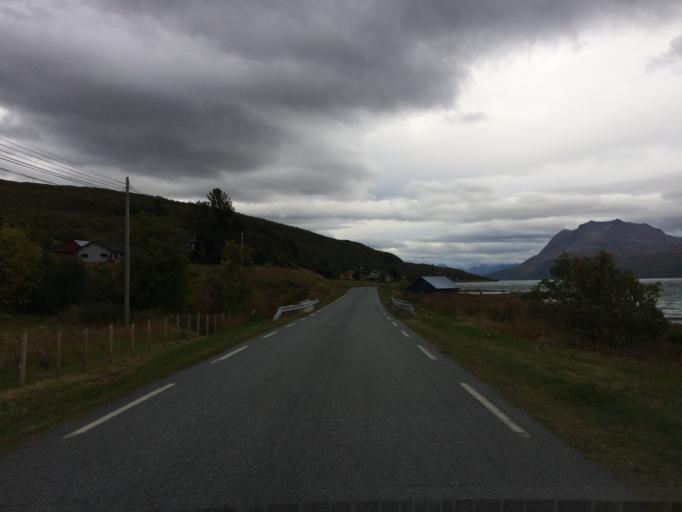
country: NO
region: Troms
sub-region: Sorreisa
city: Sorreisa
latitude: 69.5293
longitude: 18.2959
